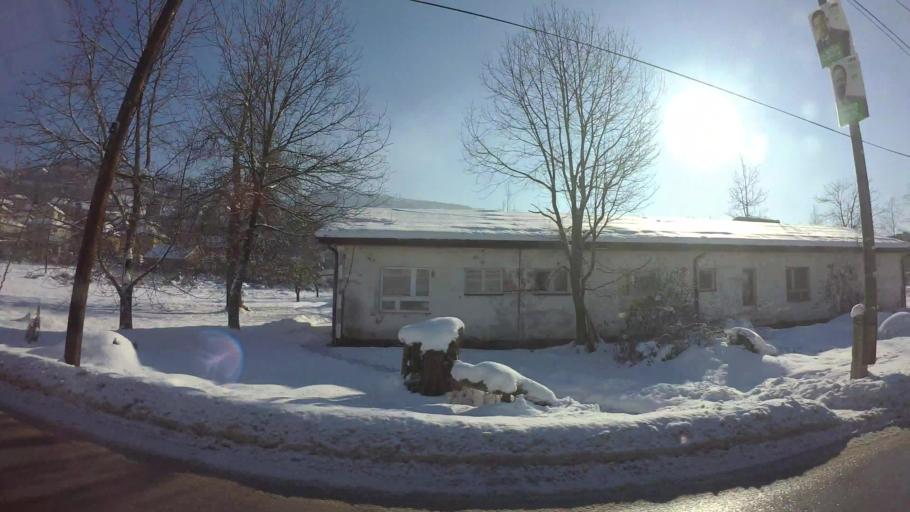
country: BA
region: Federation of Bosnia and Herzegovina
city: Kobilja Glava
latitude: 43.8823
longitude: 18.4151
